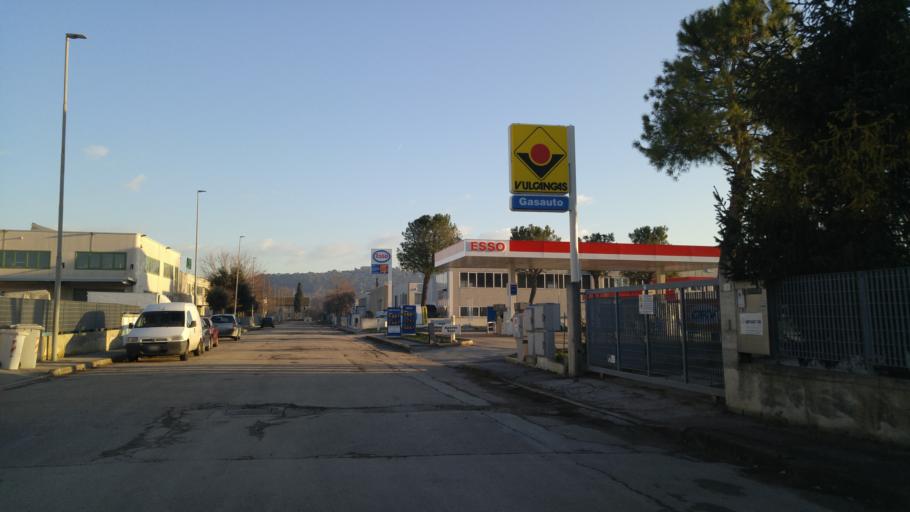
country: IT
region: The Marches
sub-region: Provincia di Ancona
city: Monterado
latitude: 43.7104
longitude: 13.0759
